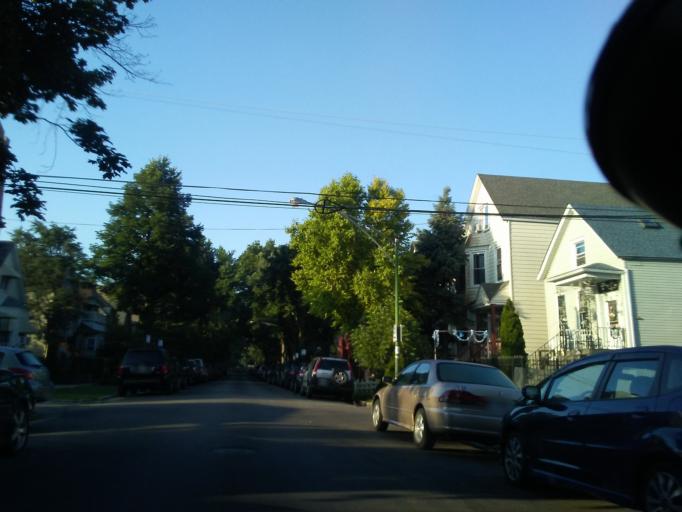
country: US
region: Illinois
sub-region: Cook County
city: Lincolnwood
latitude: 41.9316
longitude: -87.7160
